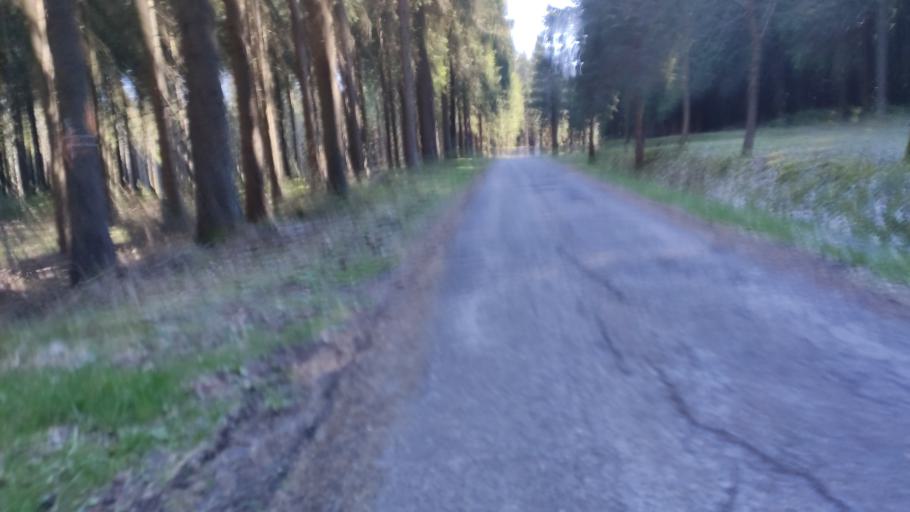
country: DE
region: Bavaria
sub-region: Upper Franconia
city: Tschirn
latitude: 50.4558
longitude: 11.4614
